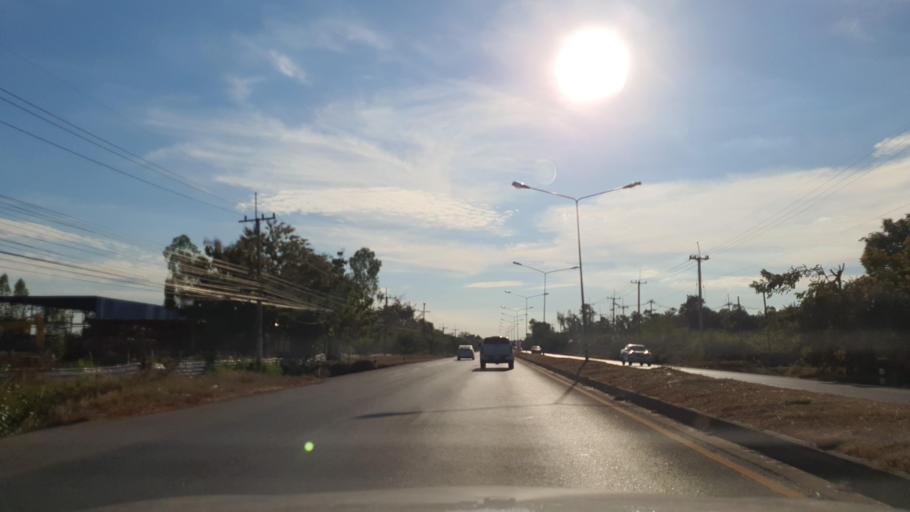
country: TH
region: Maha Sarakham
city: Kantharawichai
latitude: 16.3438
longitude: 103.3183
